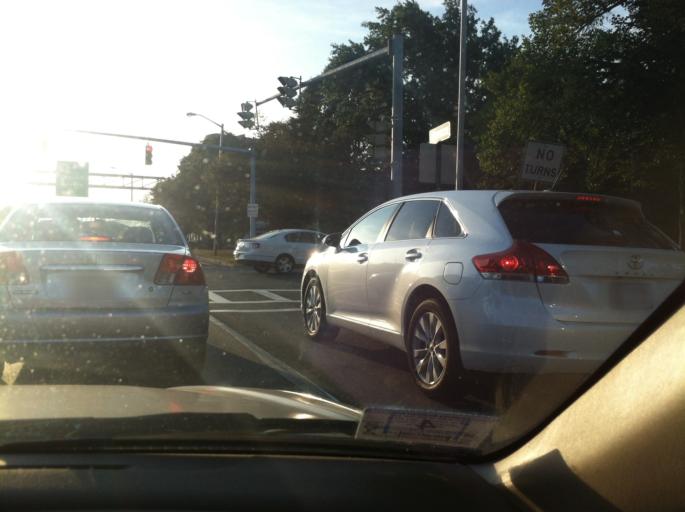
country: US
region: Massachusetts
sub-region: Middlesex County
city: Somerville
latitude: 42.4045
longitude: -71.0915
